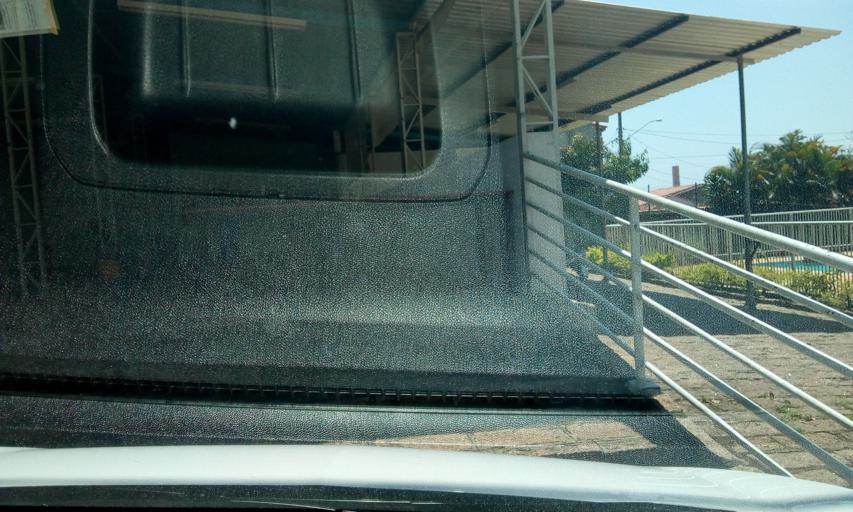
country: BR
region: Sao Paulo
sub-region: Itupeva
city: Itupeva
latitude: -23.1592
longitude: -47.0549
